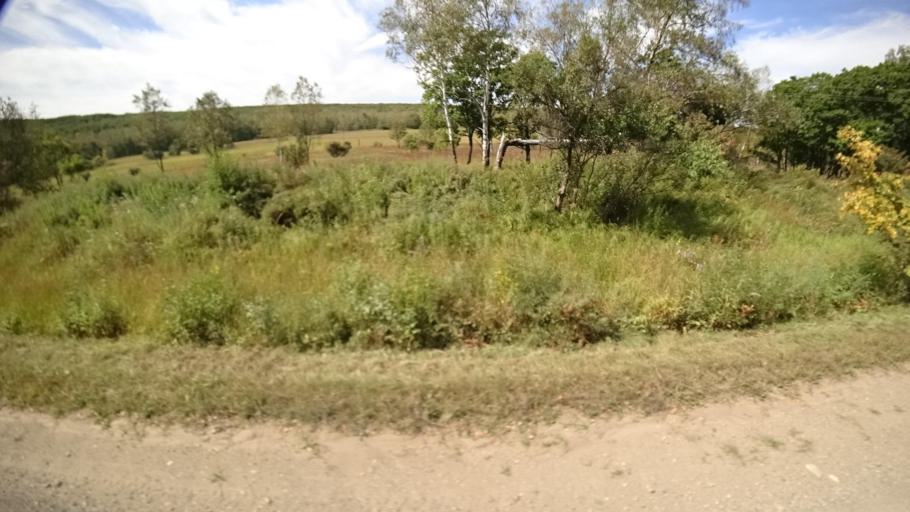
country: RU
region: Primorskiy
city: Yakovlevka
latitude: 44.6812
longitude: 133.6172
